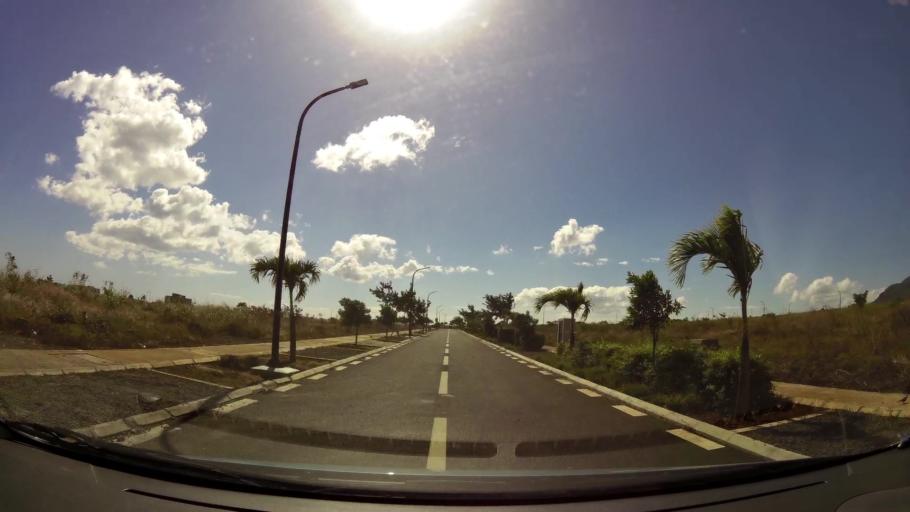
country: MU
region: Black River
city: Cascavelle
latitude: -20.2800
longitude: 57.3862
